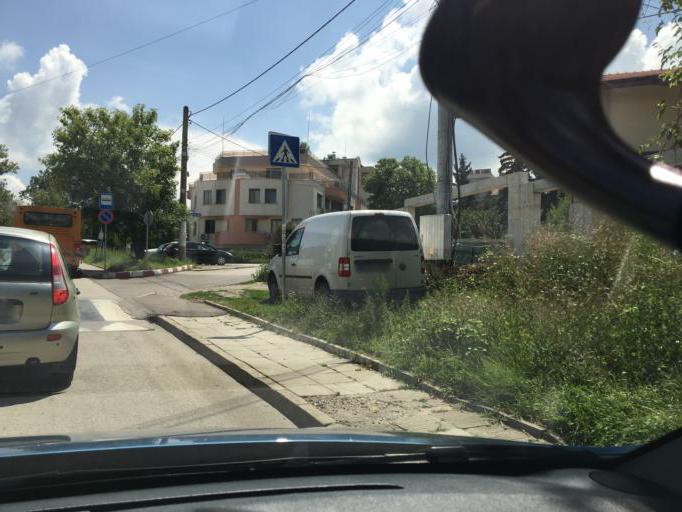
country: BG
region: Sofia-Capital
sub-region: Stolichna Obshtina
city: Sofia
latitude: 42.6229
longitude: 23.3325
